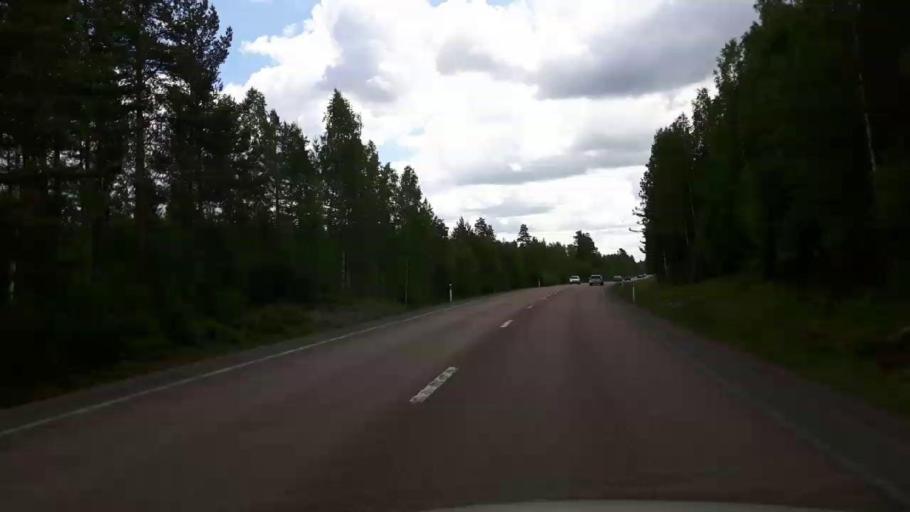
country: SE
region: Dalarna
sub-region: Saters Kommun
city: Saeter
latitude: 60.4959
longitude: 15.7573
